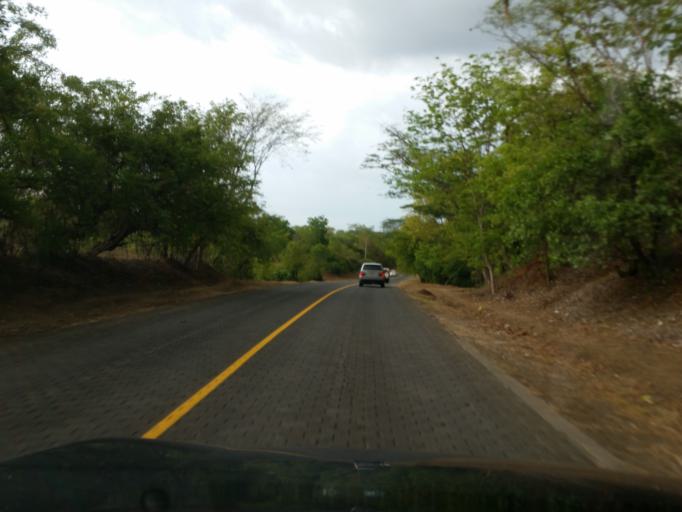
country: NI
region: Managua
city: Carlos Fonseca Amador
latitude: 11.9798
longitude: -86.5153
